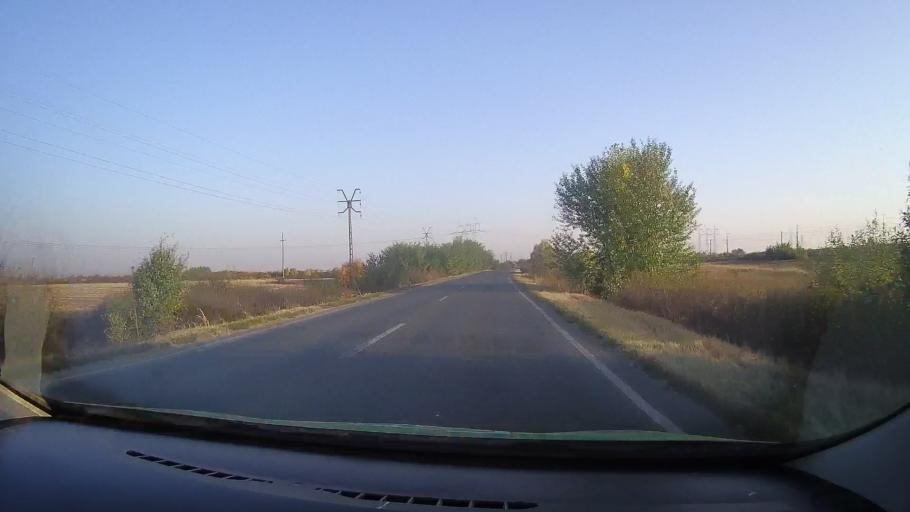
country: RO
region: Arad
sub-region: Comuna Sofronea
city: Sofronea
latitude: 46.2341
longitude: 21.3207
